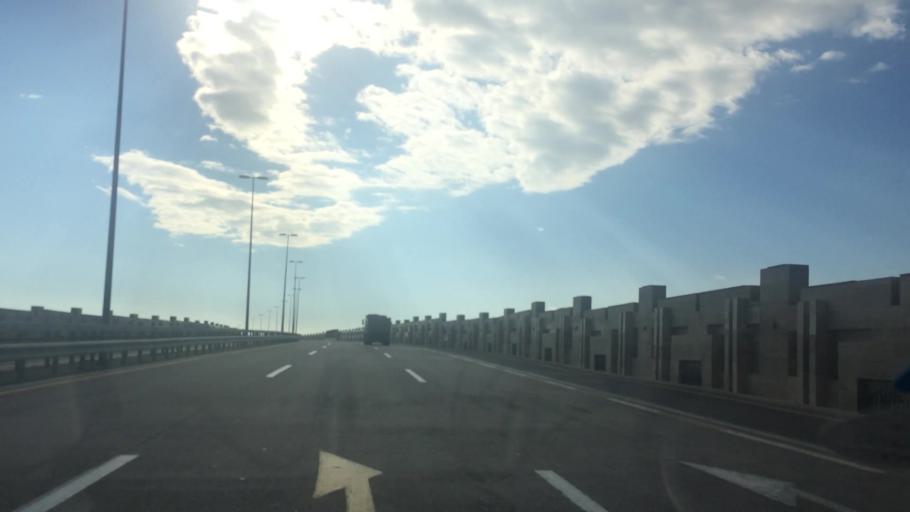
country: AZ
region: Baki
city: Hovsan
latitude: 40.3925
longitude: 50.0753
